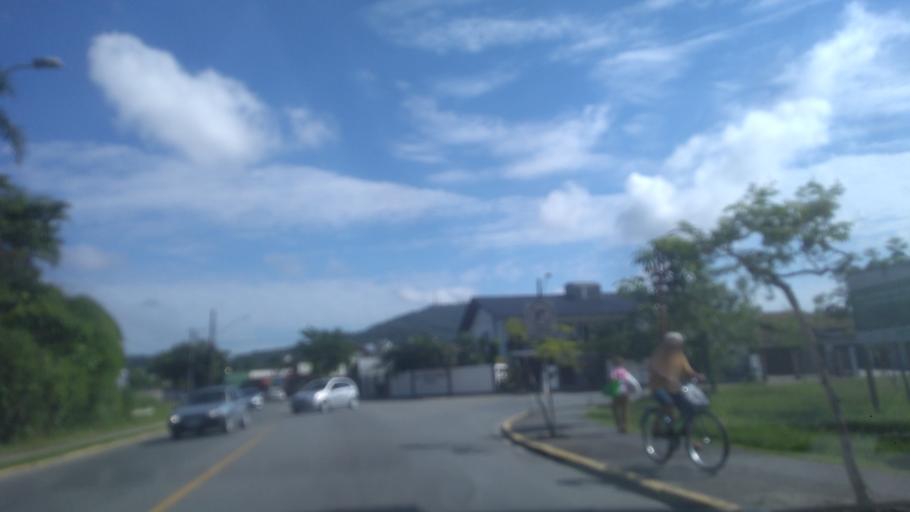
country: BR
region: Santa Catarina
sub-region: Joinville
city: Joinville
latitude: -26.3119
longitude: -48.8285
